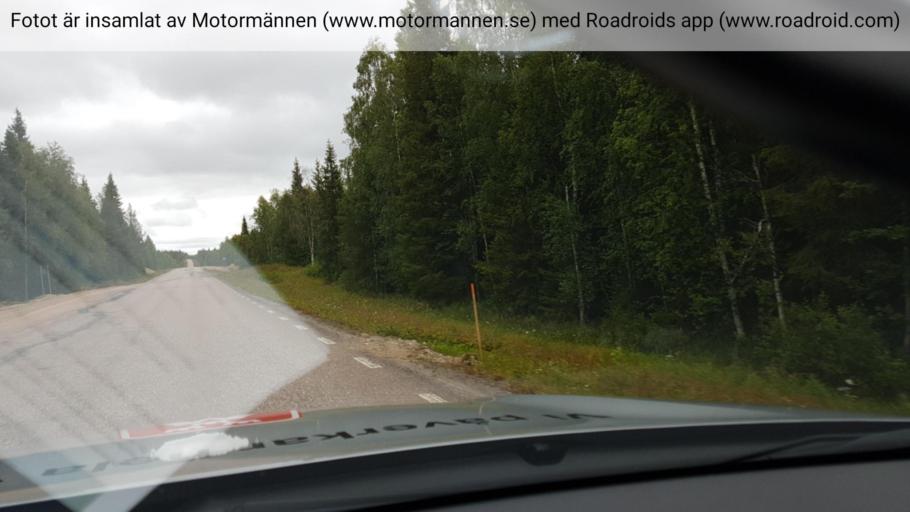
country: SE
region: Norrbotten
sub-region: Overkalix Kommun
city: OEverkalix
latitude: 67.0336
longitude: 22.0207
